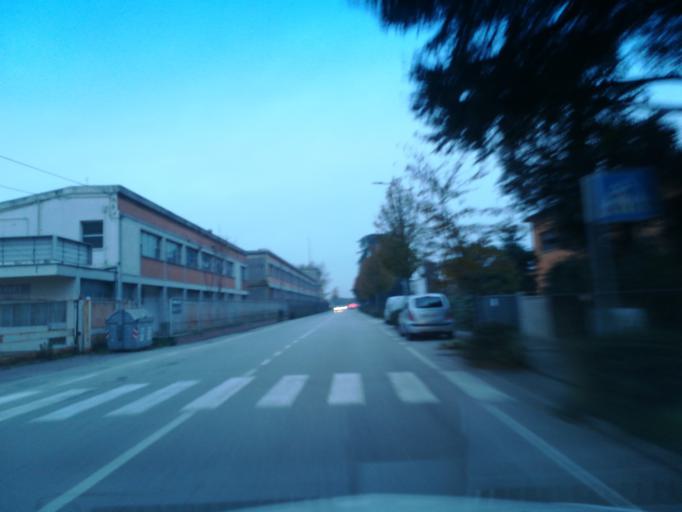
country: IT
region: Emilia-Romagna
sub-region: Provincia di Ravenna
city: Faenza
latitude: 44.2964
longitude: 11.8860
